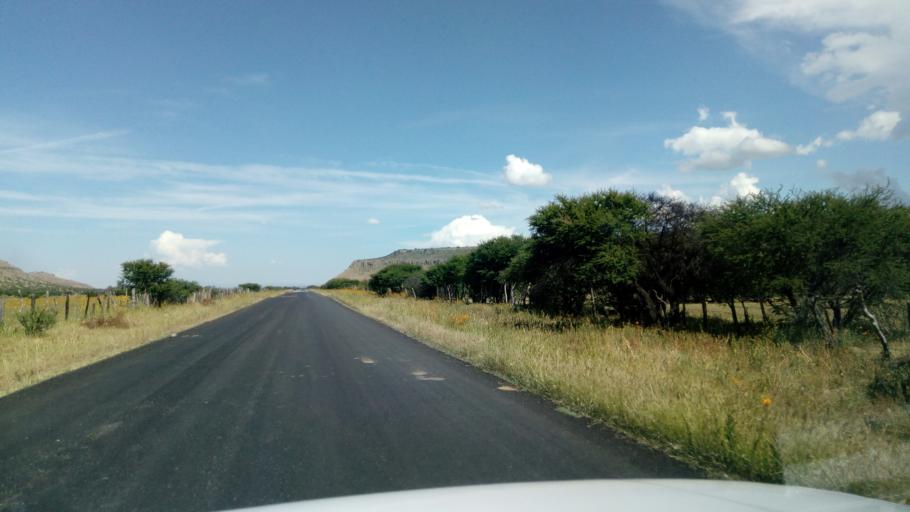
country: MX
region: Durango
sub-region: Durango
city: Jose Refugio Salcido
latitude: 23.8041
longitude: -104.4843
